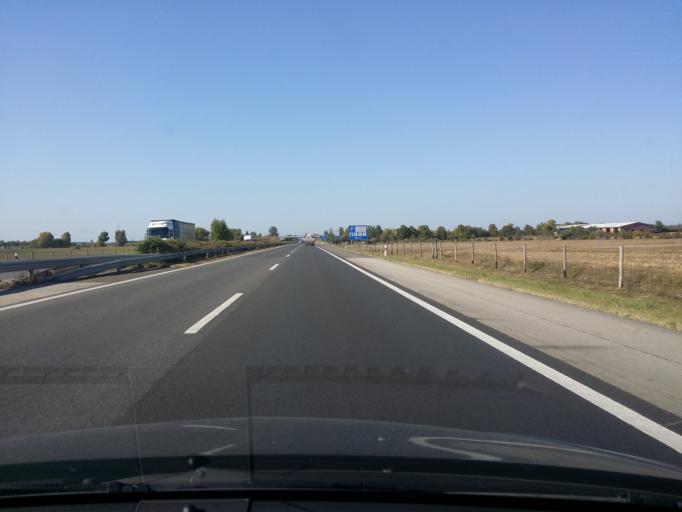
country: HU
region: Bacs-Kiskun
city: Lajosmizse
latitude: 47.0350
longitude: 19.5737
